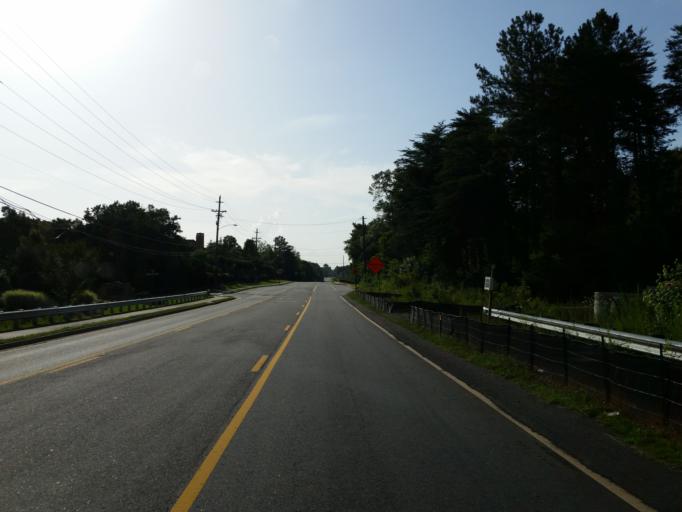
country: US
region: Georgia
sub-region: Cherokee County
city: Woodstock
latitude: 34.0684
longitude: -84.4722
